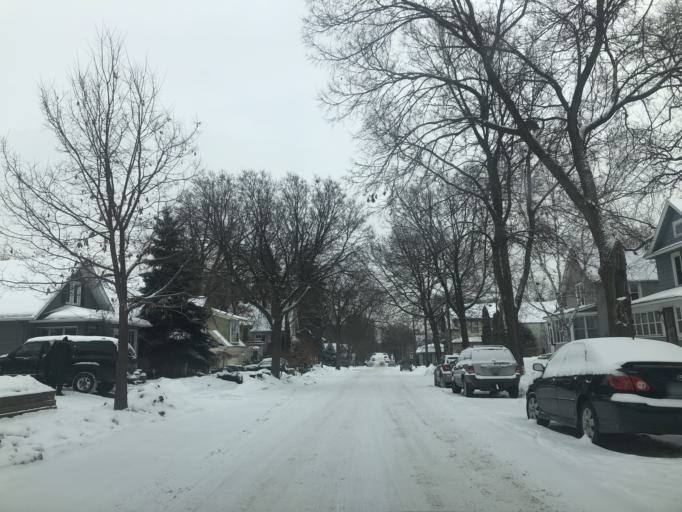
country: US
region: Minnesota
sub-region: Hennepin County
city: Richfield
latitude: 44.9323
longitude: -93.2812
